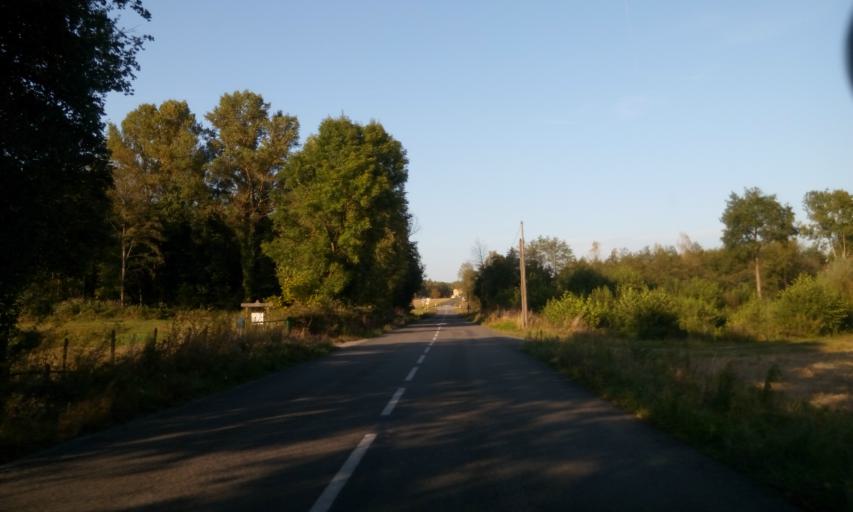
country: FR
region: Rhone-Alpes
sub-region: Departement de l'Ain
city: Priay
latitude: 46.0253
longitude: 5.2896
